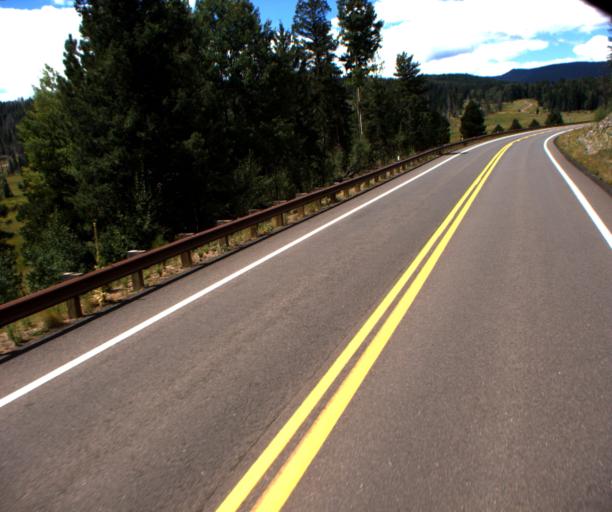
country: US
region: Arizona
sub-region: Apache County
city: Eagar
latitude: 33.9294
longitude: -109.4744
